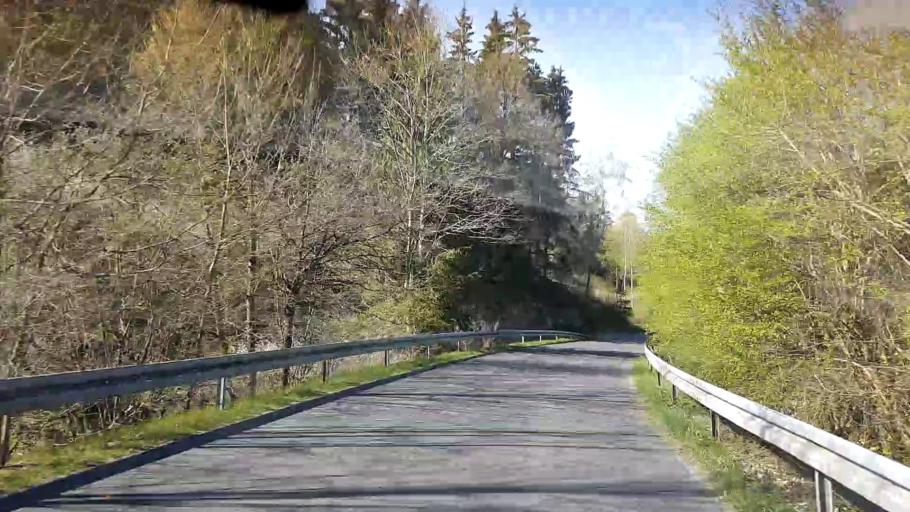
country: DE
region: Bavaria
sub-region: Upper Franconia
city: Waischenfeld
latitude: 49.8284
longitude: 11.3511
